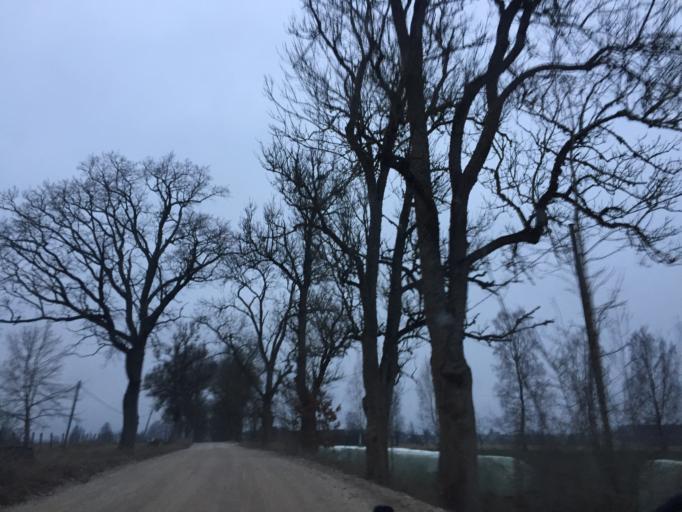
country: LV
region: Raunas
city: Rauna
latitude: 57.3379
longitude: 25.5956
